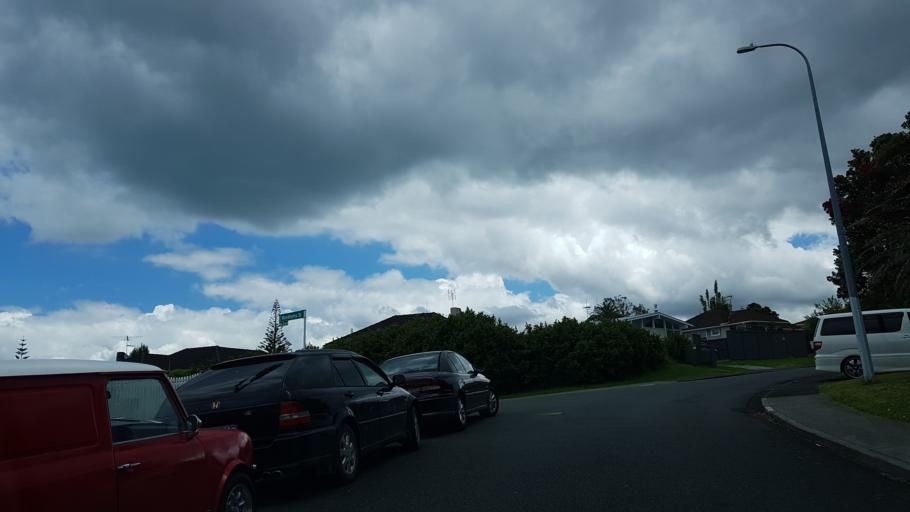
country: NZ
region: Auckland
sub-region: Auckland
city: North Shore
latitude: -36.7935
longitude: 174.6959
